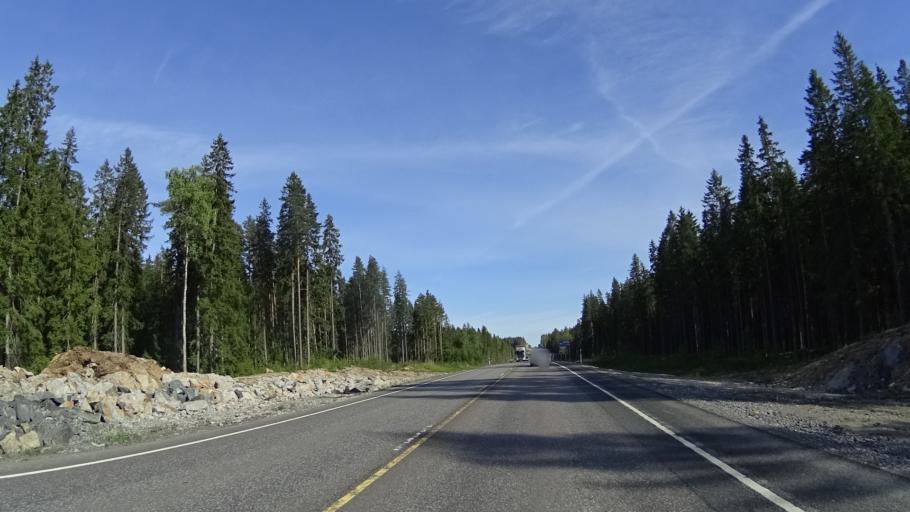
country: FI
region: Haeme
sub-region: Forssa
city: Tammela
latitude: 60.7089
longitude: 23.7668
